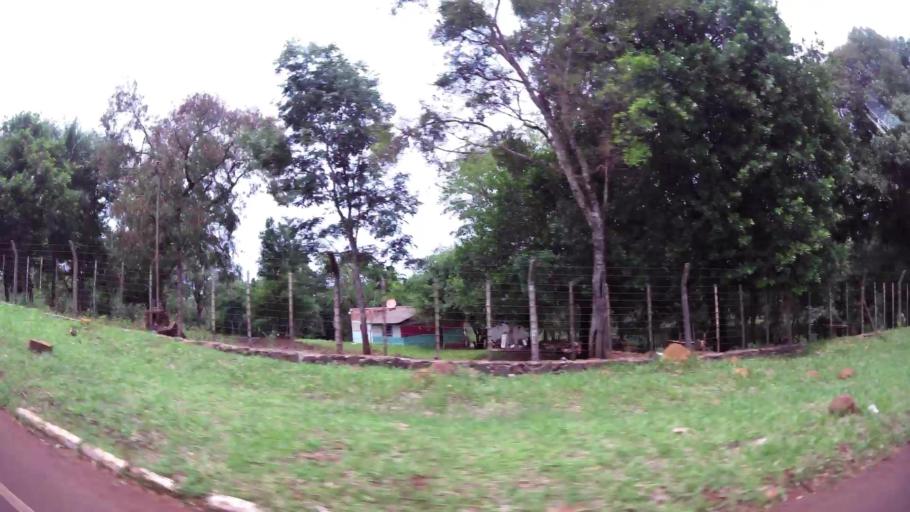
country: PY
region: Alto Parana
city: Presidente Franco
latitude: -25.5591
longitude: -54.6311
